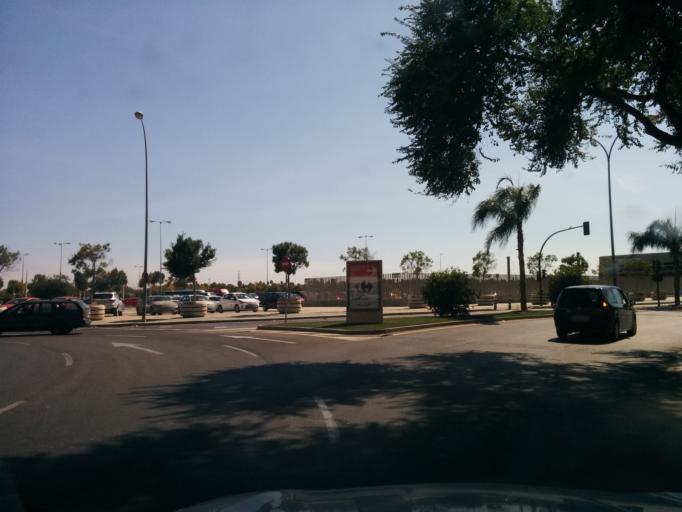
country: ES
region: Andalusia
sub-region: Provincia de Sevilla
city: San Juan de Aznalfarache
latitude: 37.3742
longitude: -6.0095
